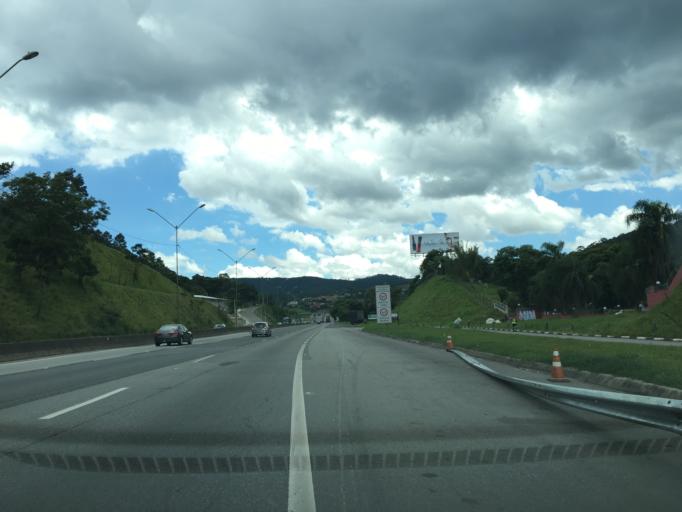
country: BR
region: Sao Paulo
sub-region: Mairipora
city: Mairipora
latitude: -23.3333
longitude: -46.5765
